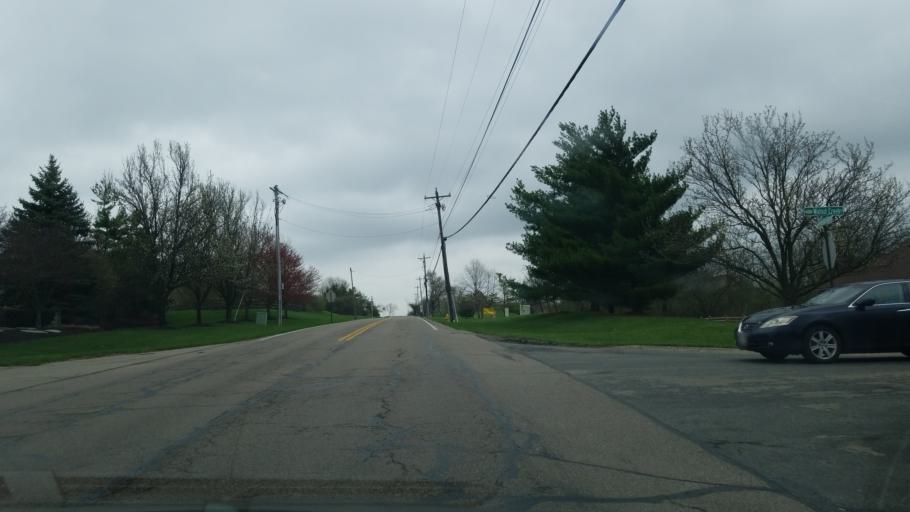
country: US
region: Ohio
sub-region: Butler County
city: Beckett Ridge
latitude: 39.3735
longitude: -84.4508
